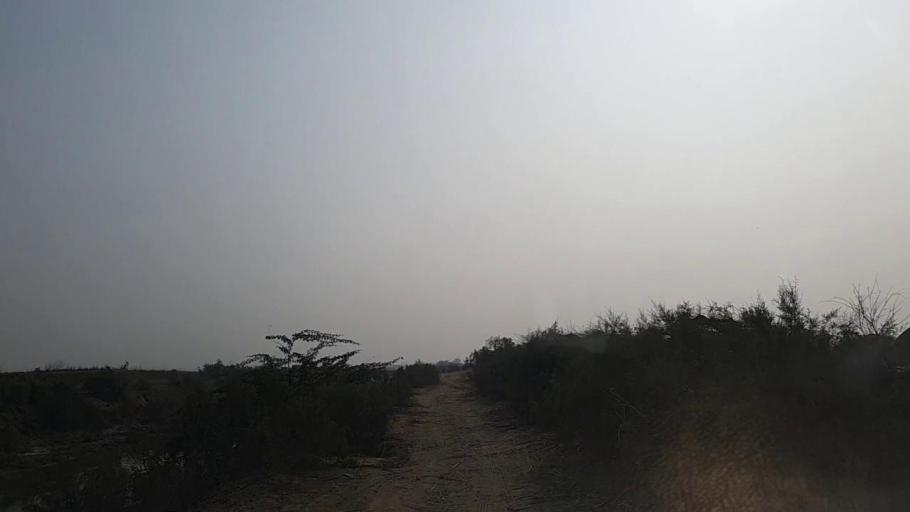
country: PK
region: Sindh
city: Sanghar
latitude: 26.0865
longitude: 68.9142
